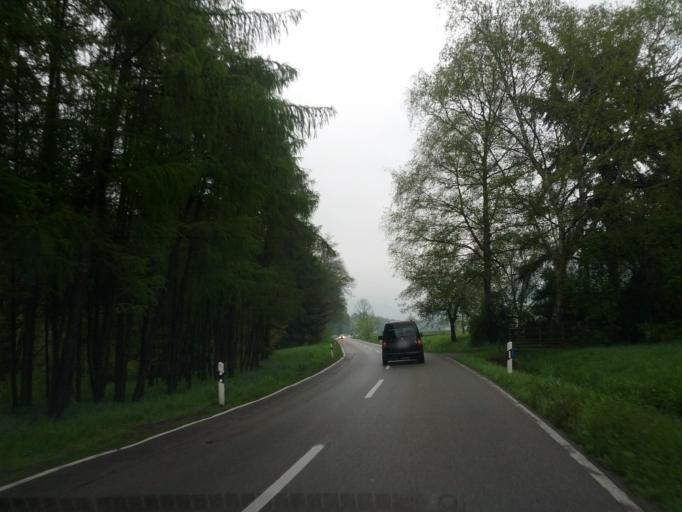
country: DE
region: Baden-Wuerttemberg
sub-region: Freiburg Region
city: Muenstertal/Schwarzwald
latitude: 47.8679
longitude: 7.7432
